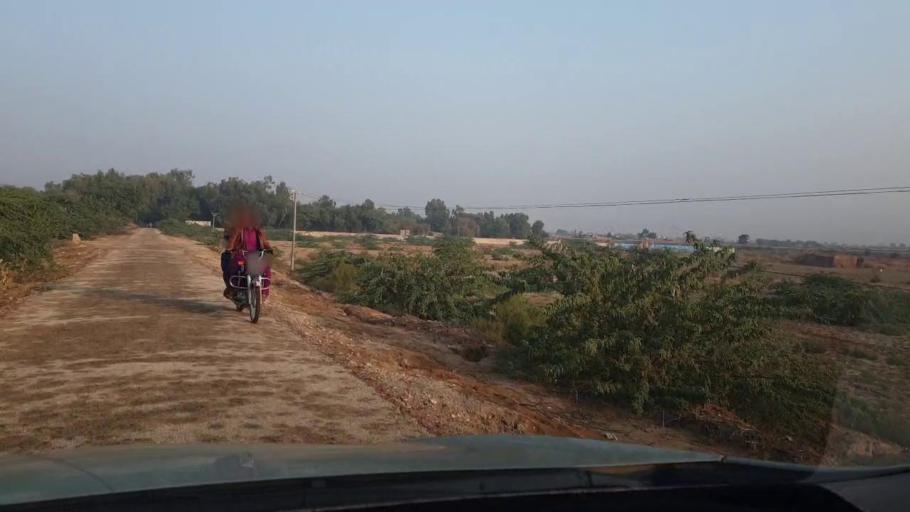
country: PK
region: Sindh
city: Sehwan
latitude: 26.3936
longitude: 67.8632
